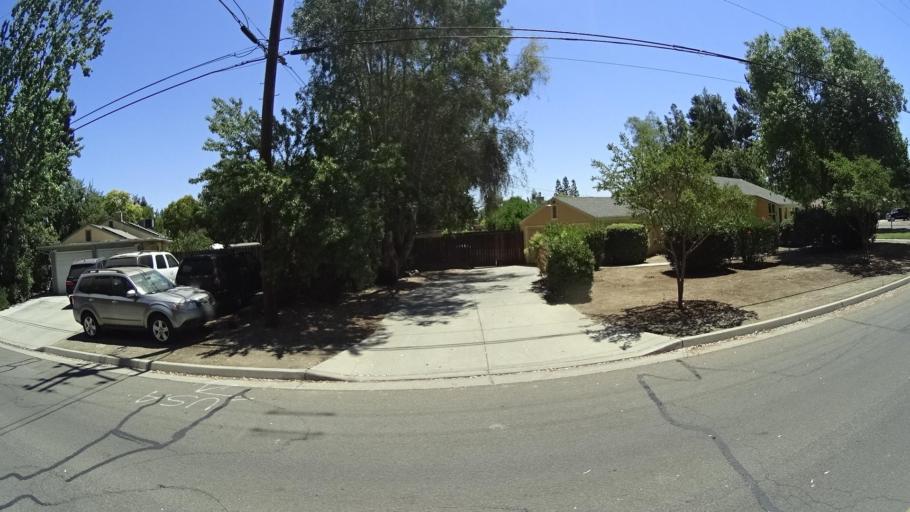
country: US
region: California
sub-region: Fresno County
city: Fresno
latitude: 36.7900
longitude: -119.8024
